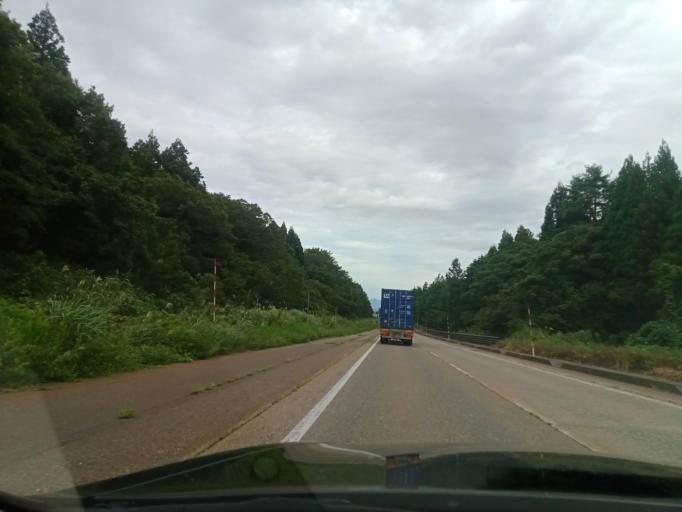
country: JP
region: Niigata
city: Arai
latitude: 37.0011
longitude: 138.2235
